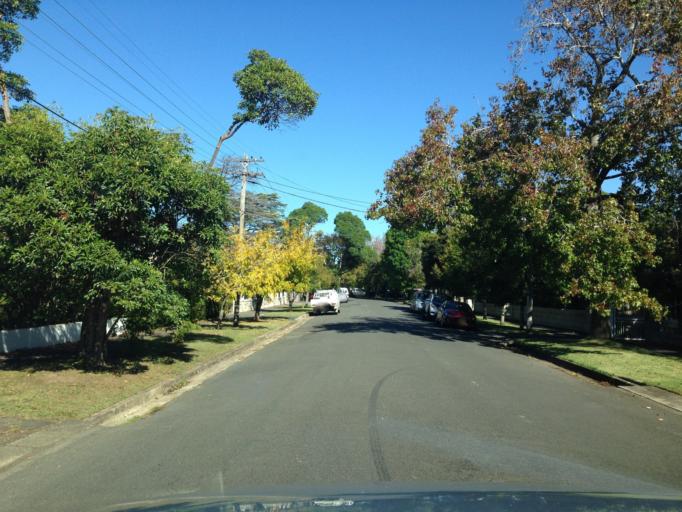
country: AU
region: New South Wales
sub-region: Ku-ring-gai
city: Killara
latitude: -33.7639
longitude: 151.1685
